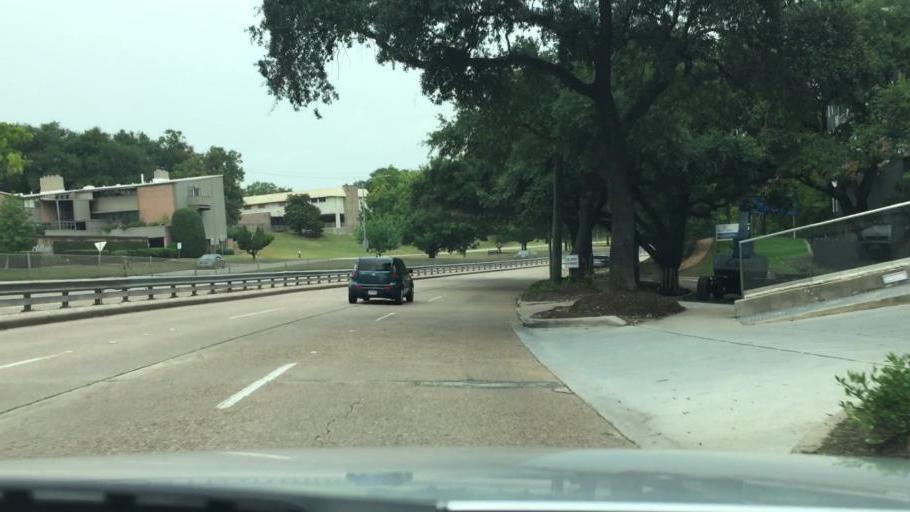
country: US
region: Texas
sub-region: Harris County
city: West University Place
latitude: 29.7608
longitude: -95.4142
